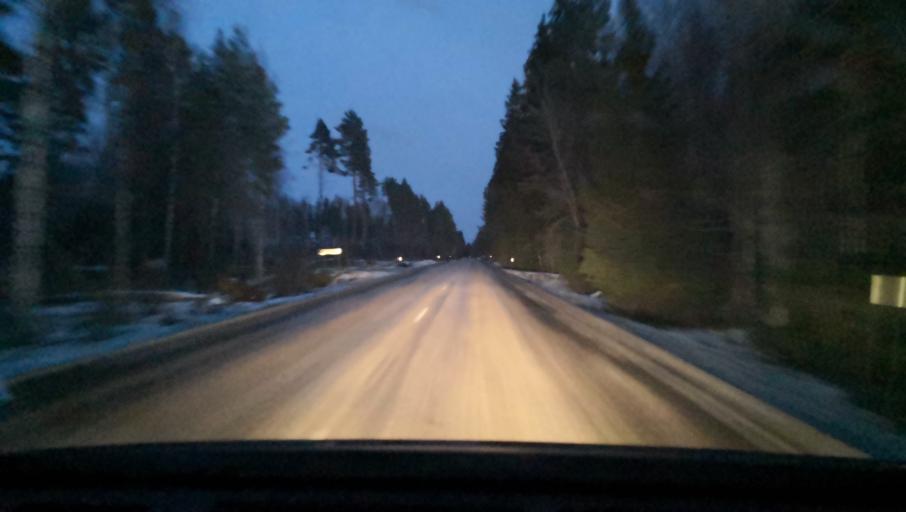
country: SE
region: Vaestmanland
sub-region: Sala Kommun
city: Sala
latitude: 59.8390
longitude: 16.4981
